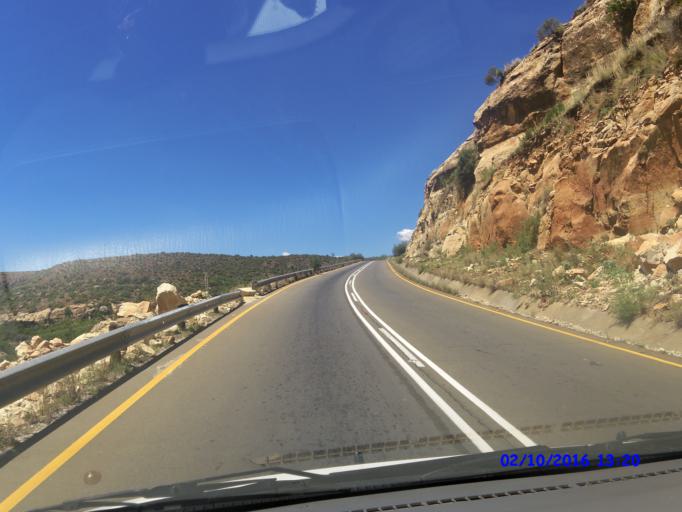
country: LS
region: Maseru
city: Nako
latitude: -29.4213
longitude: 27.6996
